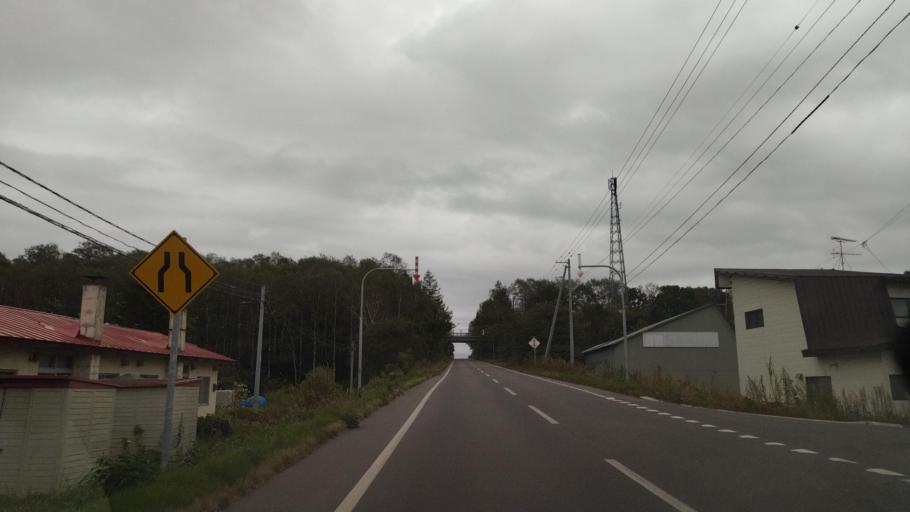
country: JP
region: Hokkaido
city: Otofuke
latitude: 43.2341
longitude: 143.3000
